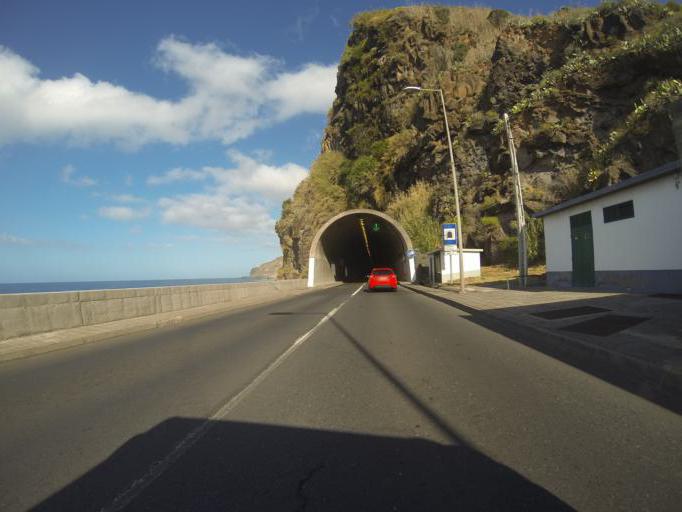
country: PT
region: Madeira
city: Ponta do Sol
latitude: 32.6786
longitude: -17.0818
